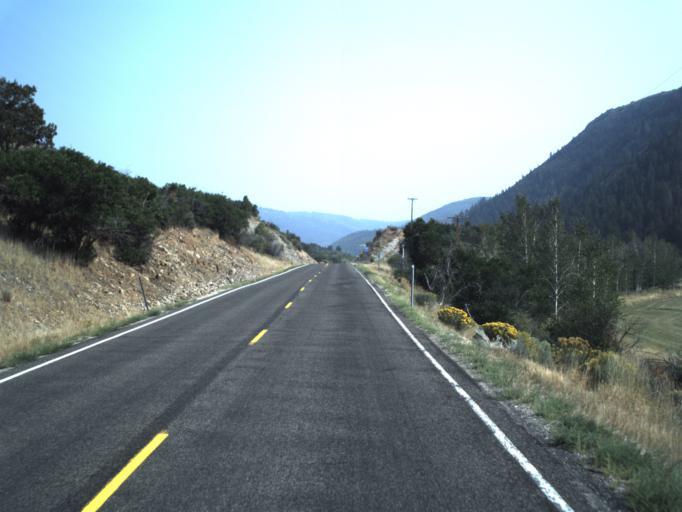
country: US
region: Utah
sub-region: Summit County
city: Kamas
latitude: 40.6306
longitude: -111.2503
